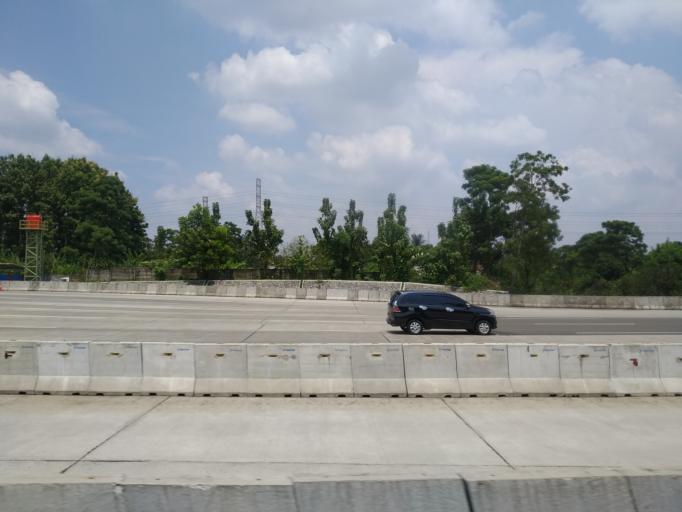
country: ID
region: West Java
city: Bogor
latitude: -6.5962
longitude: 106.8268
